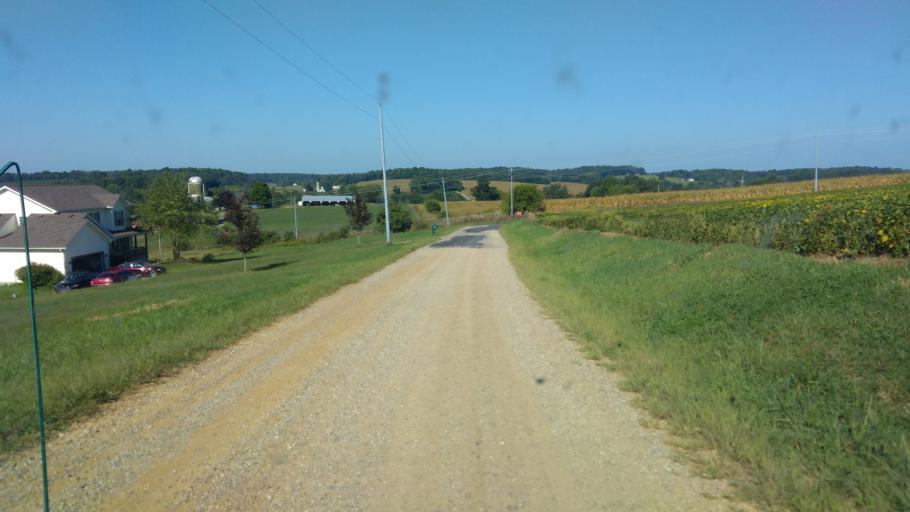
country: US
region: Ohio
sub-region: Knox County
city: Fredericktown
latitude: 40.4887
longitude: -82.4529
